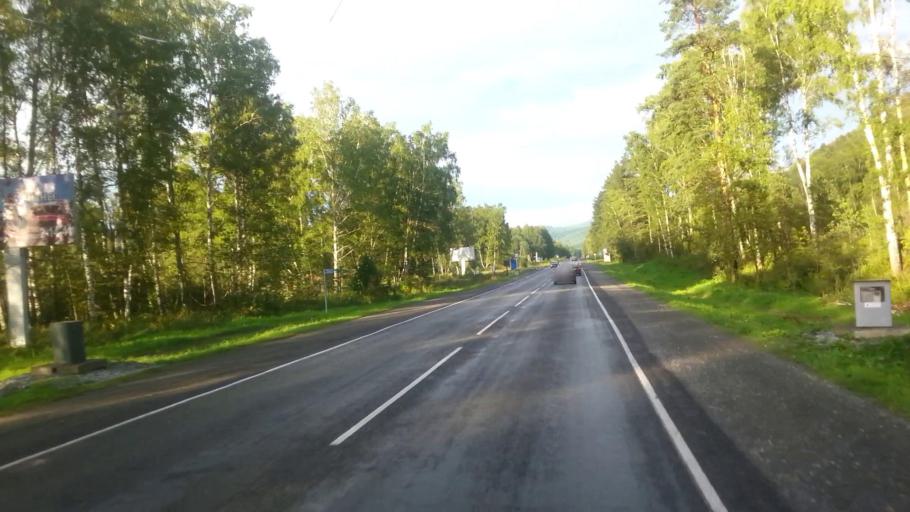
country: RU
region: Altay
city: Souzga
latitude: 51.8734
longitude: 85.7984
